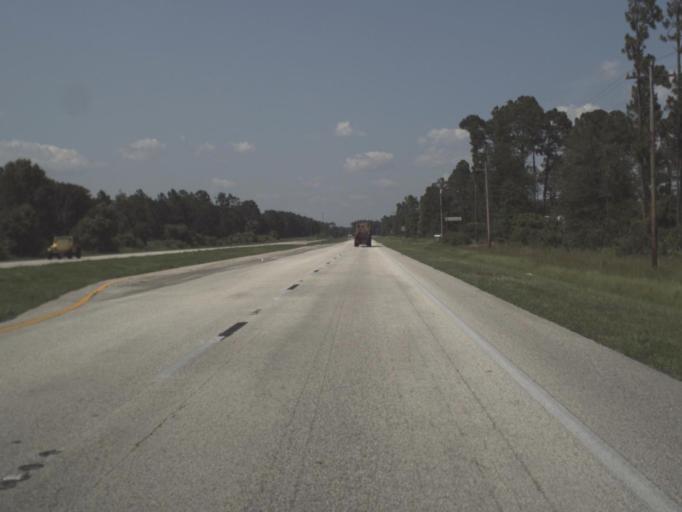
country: US
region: Florida
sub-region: Alachua County
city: Hawthorne
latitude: 29.5636
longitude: -82.0942
